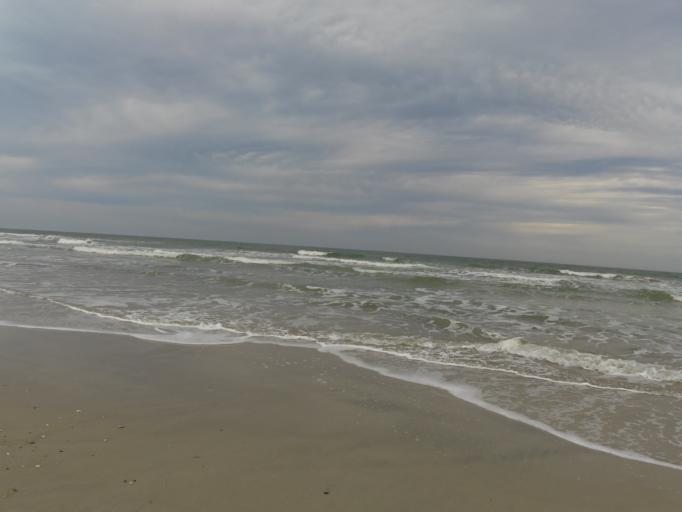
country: US
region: Florida
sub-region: Duval County
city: Neptune Beach
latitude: 30.3144
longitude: -81.3928
